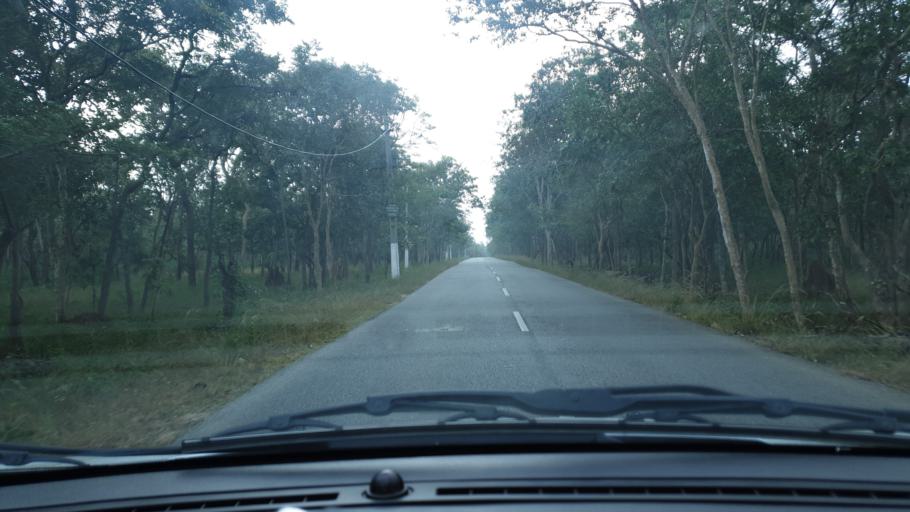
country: IN
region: Andhra Pradesh
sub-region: Kurnool
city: Srisailam
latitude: 16.2950
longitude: 78.7309
